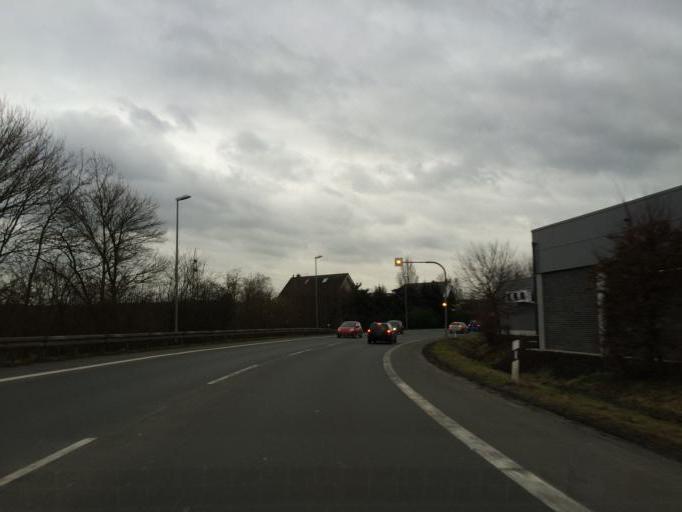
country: DE
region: North Rhine-Westphalia
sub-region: Regierungsbezirk Munster
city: Haltern
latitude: 51.7350
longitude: 7.1895
